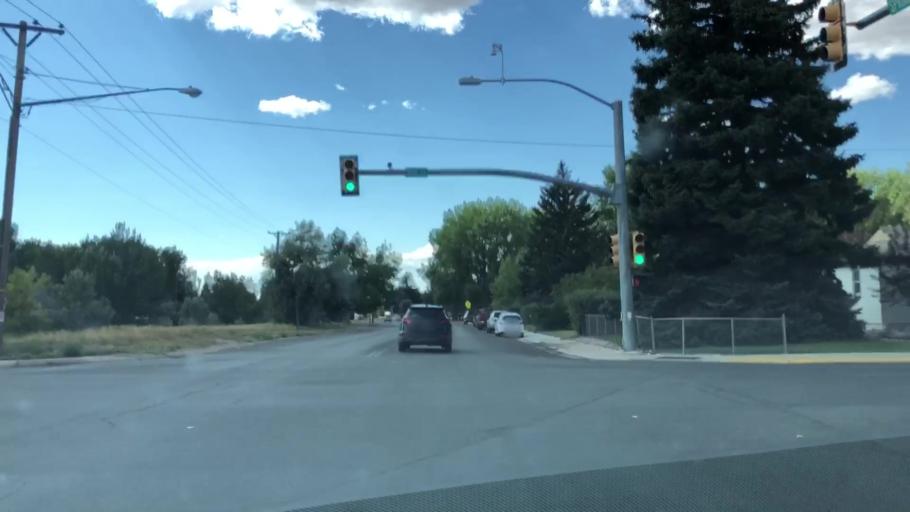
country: US
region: Wyoming
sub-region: Albany County
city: Laramie
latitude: 41.3029
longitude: -105.5784
